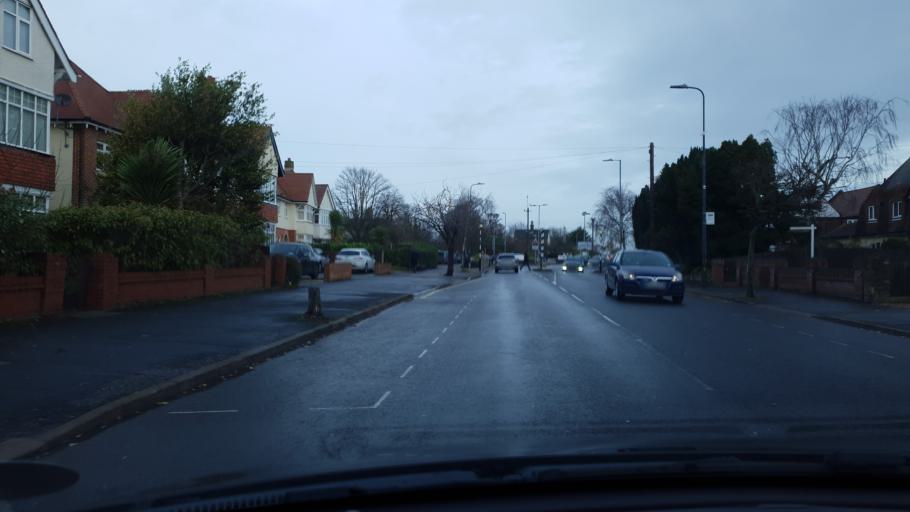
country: GB
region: England
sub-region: Essex
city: Frinton-on-Sea
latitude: 51.8363
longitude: 1.2446
